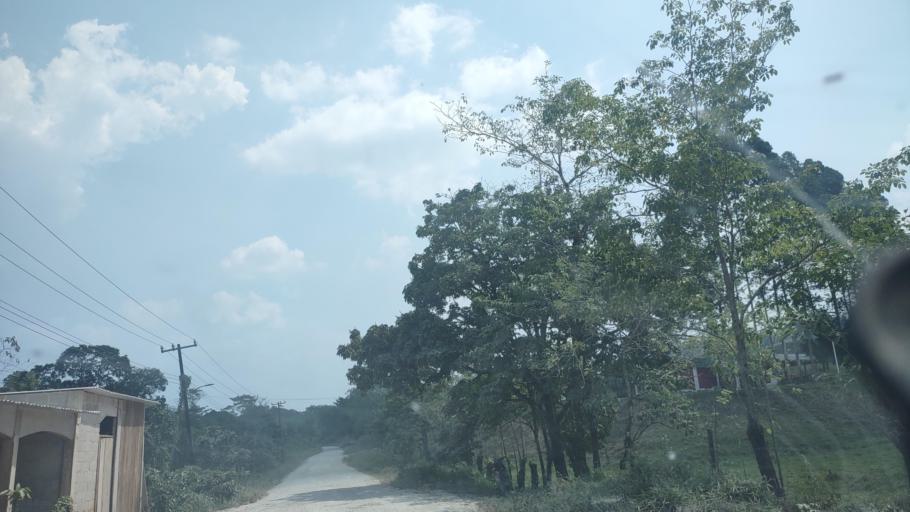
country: MX
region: Tabasco
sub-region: Huimanguillo
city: Francisco Rueda
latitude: 17.5995
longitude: -93.8998
